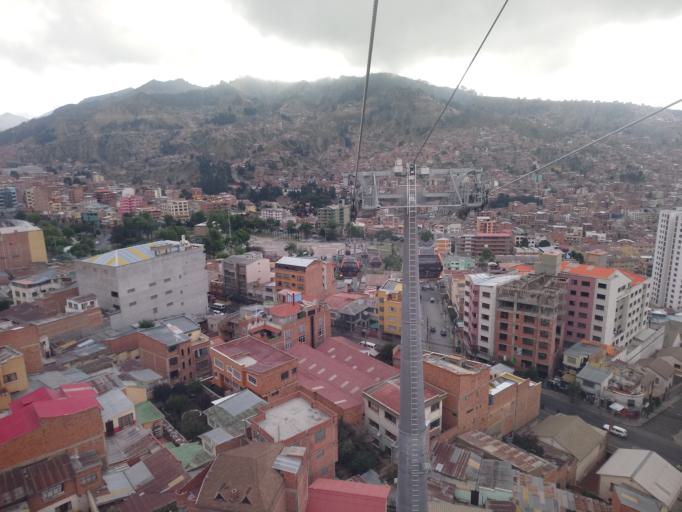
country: BO
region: La Paz
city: La Paz
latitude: -16.4852
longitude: -68.1246
